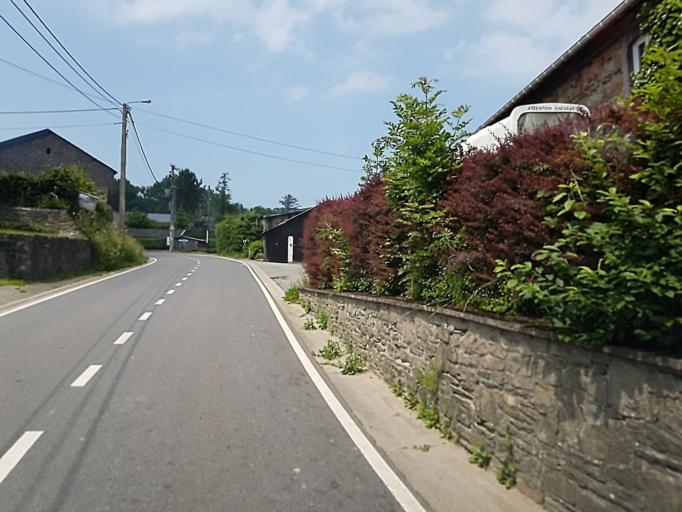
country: BE
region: Wallonia
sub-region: Province de Liege
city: Lierneux
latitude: 50.3222
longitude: 5.7369
